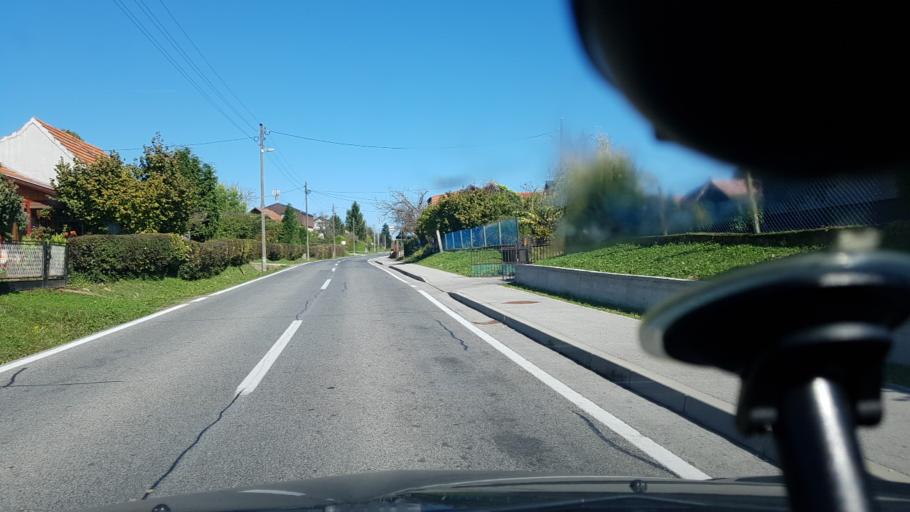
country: HR
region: Zagrebacka
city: Kriz
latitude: 45.7188
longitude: 16.5013
